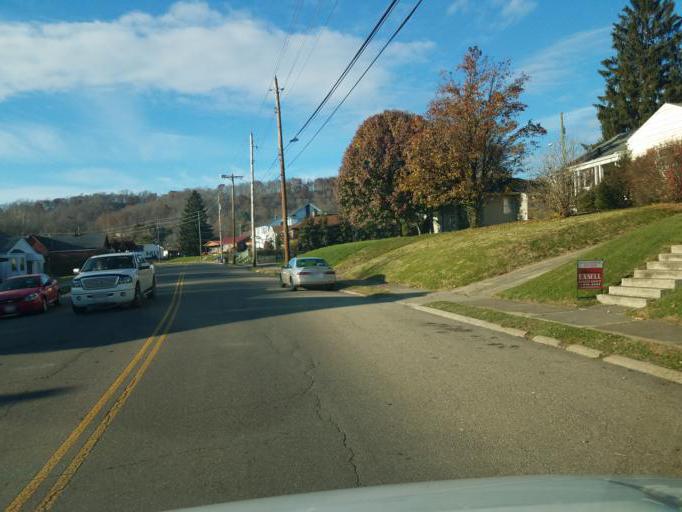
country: US
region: Ohio
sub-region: Scioto County
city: Rosemount
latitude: 38.7577
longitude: -82.9768
